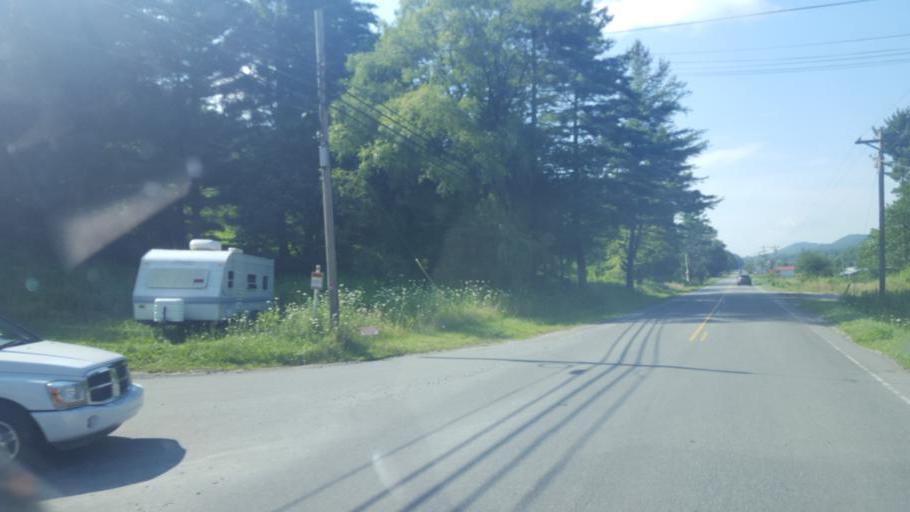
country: US
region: North Carolina
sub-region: Avery County
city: Newland
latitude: 36.1139
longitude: -81.9325
